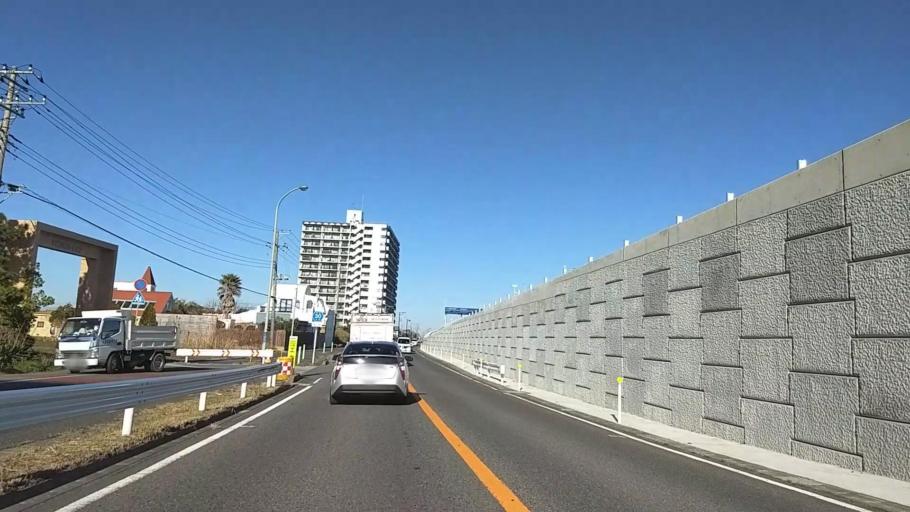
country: JP
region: Chiba
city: Togane
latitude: 35.4509
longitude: 140.4030
